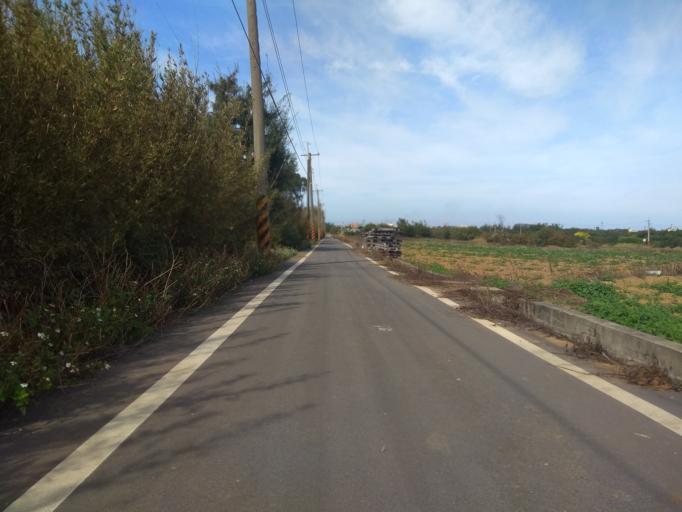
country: TW
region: Taiwan
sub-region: Hsinchu
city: Zhubei
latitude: 25.0122
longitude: 121.0787
